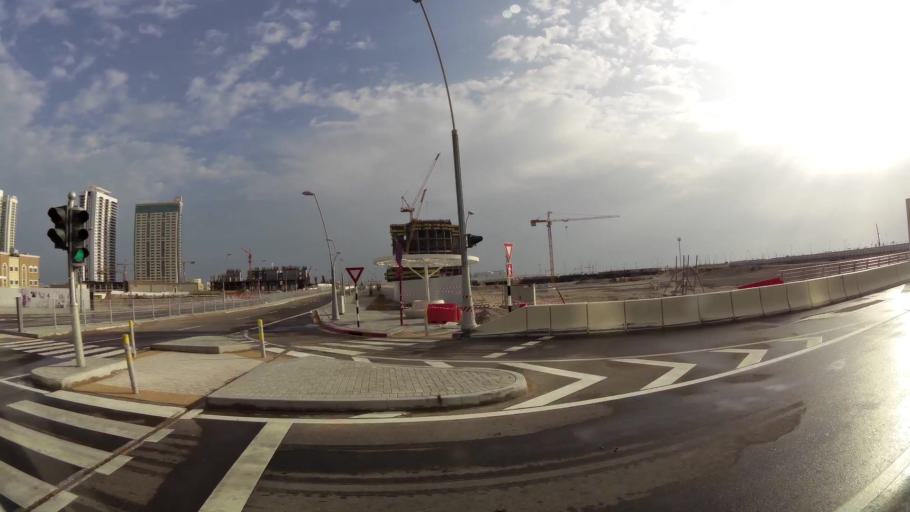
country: AE
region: Abu Dhabi
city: Abu Dhabi
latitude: 24.5056
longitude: 54.4072
